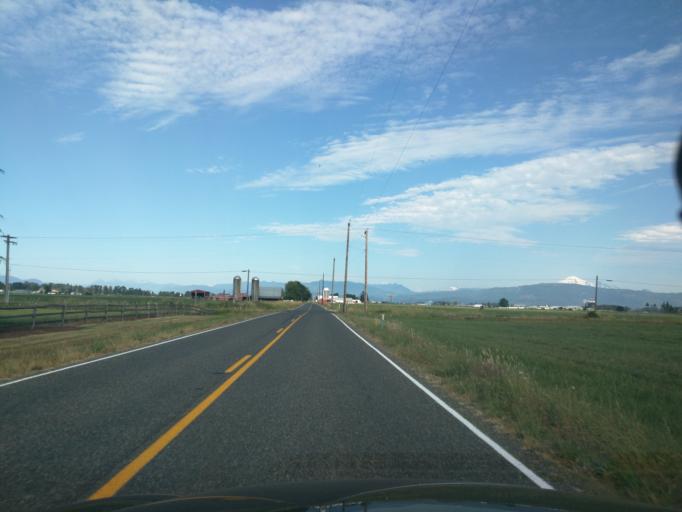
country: US
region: Washington
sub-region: Whatcom County
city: Lynden
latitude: 48.9934
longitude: -122.5027
